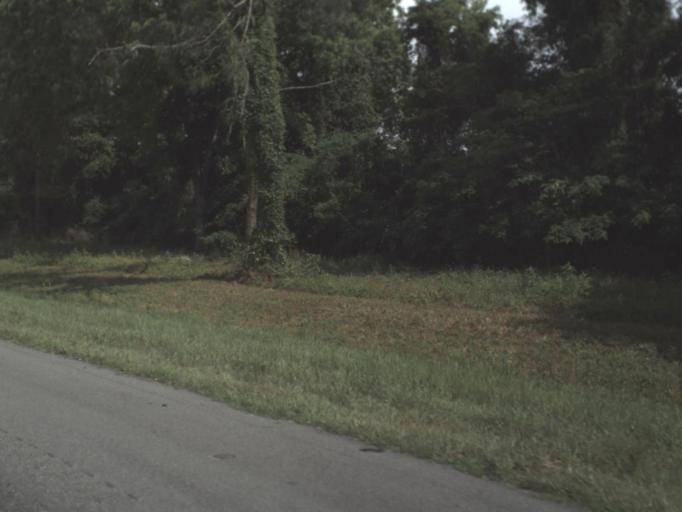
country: US
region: Florida
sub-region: Suwannee County
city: Wellborn
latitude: 30.2737
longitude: -82.7925
